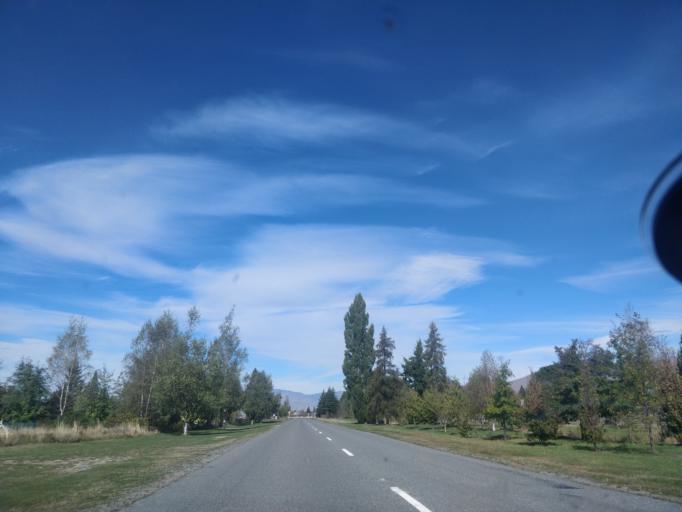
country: NZ
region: Canterbury
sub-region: Timaru District
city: Pleasant Point
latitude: -44.2542
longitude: 170.1034
